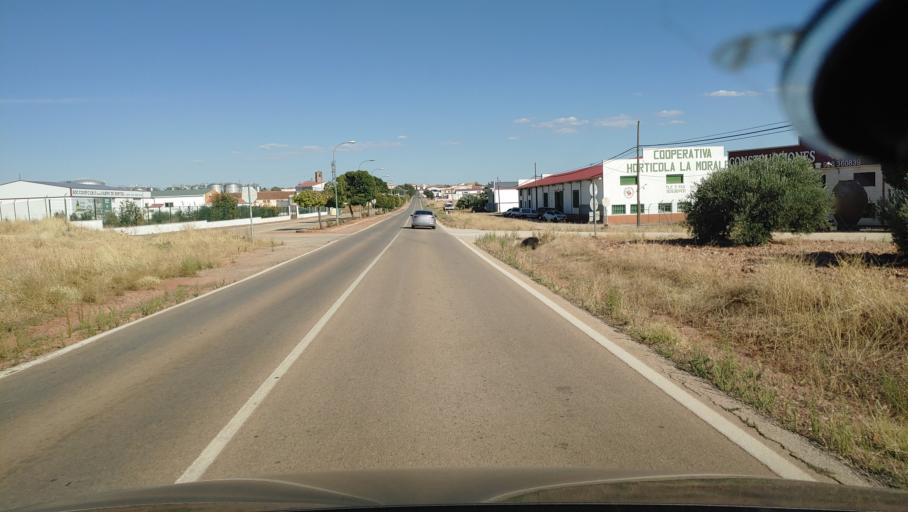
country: ES
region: Castille-La Mancha
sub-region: Provincia de Ciudad Real
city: Infantes
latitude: 38.7388
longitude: -3.0269
